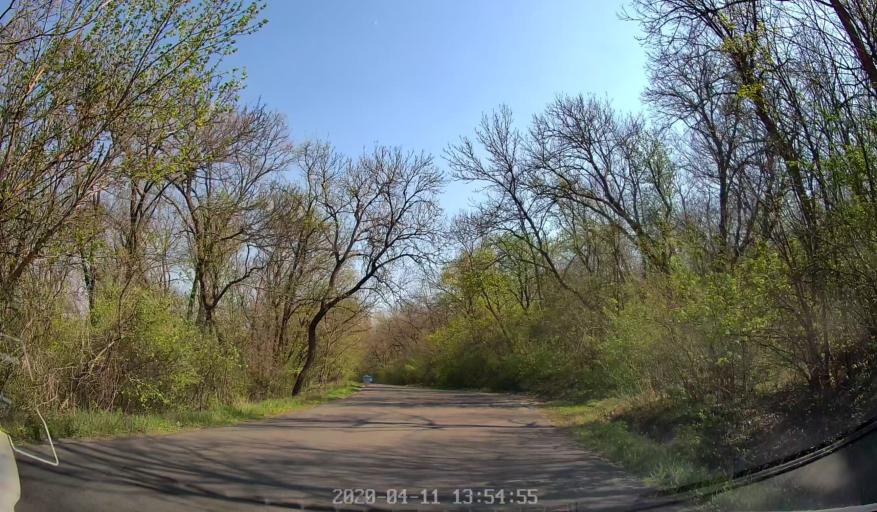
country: MD
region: Chisinau
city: Vadul lui Voda
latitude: 47.0732
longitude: 29.1071
